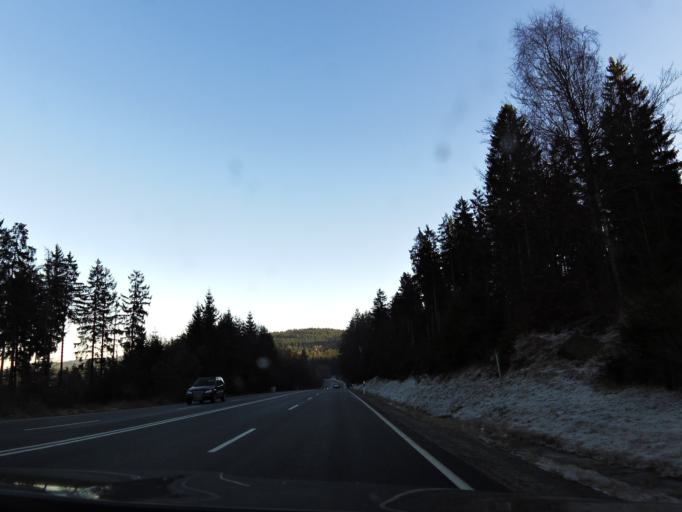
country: DE
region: Bavaria
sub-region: Upper Franconia
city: Nagel
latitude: 50.0048
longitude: 11.9074
